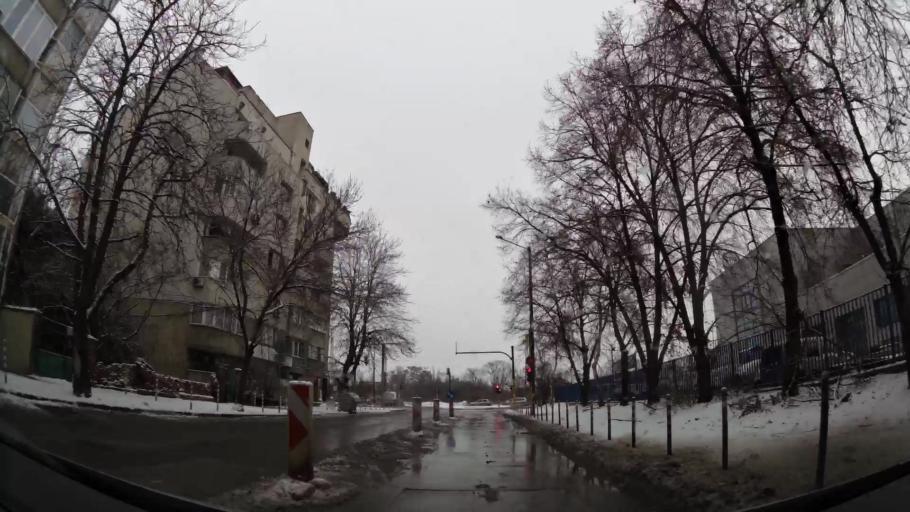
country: BG
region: Sofia-Capital
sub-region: Stolichna Obshtina
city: Sofia
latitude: 42.6987
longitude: 23.3472
